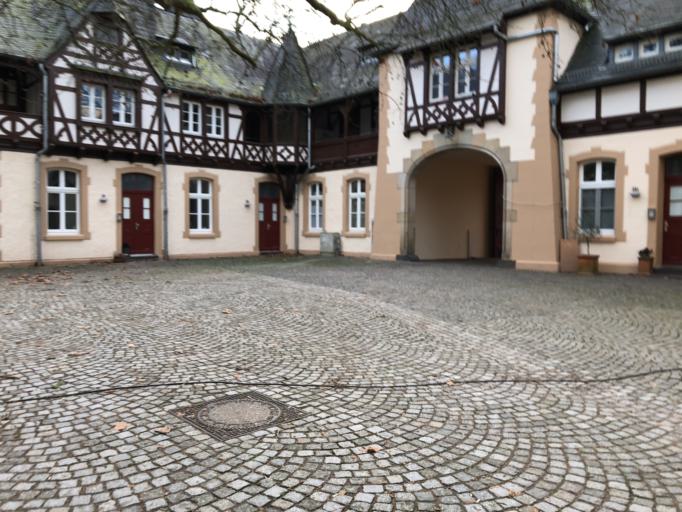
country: DE
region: North Rhine-Westphalia
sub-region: Regierungsbezirk Dusseldorf
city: Erkrath
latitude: 51.1949
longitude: 6.8484
